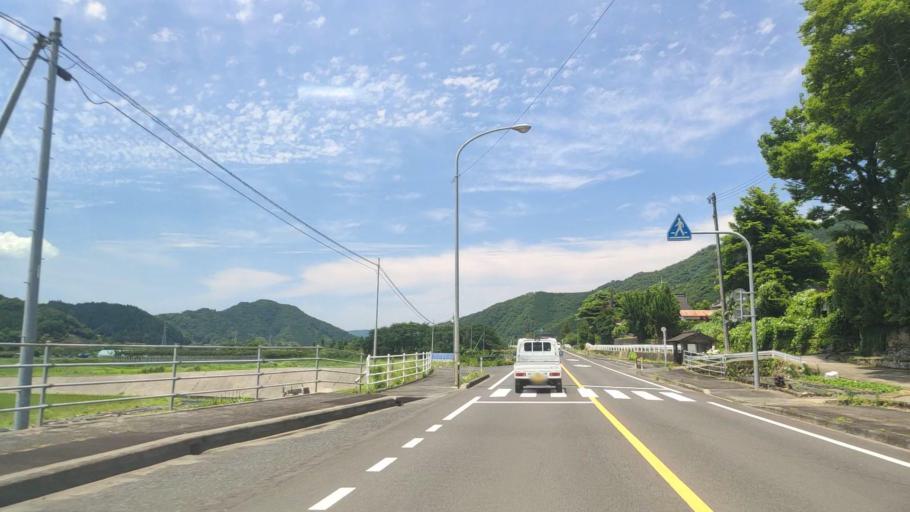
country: JP
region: Tottori
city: Tottori
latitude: 35.3685
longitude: 134.3119
